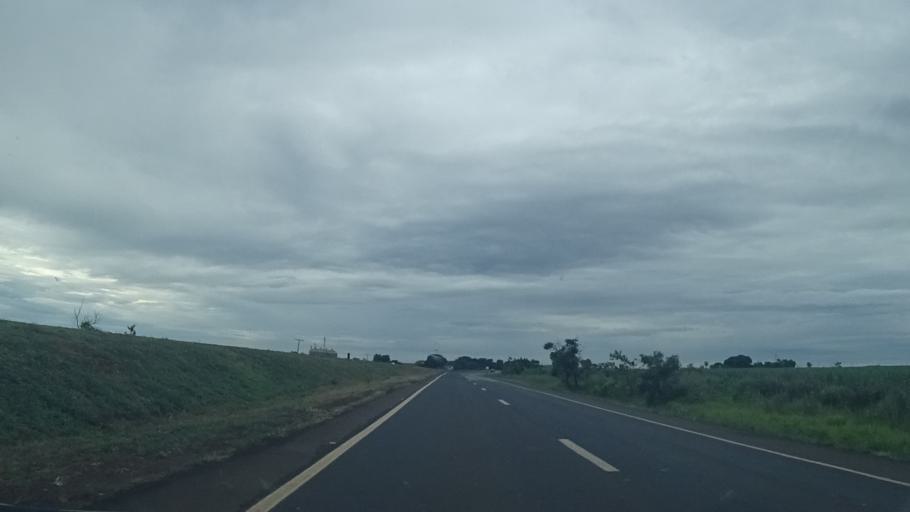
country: BR
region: Goias
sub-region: Goiatuba
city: Goiatuba
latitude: -18.1754
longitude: -49.2902
